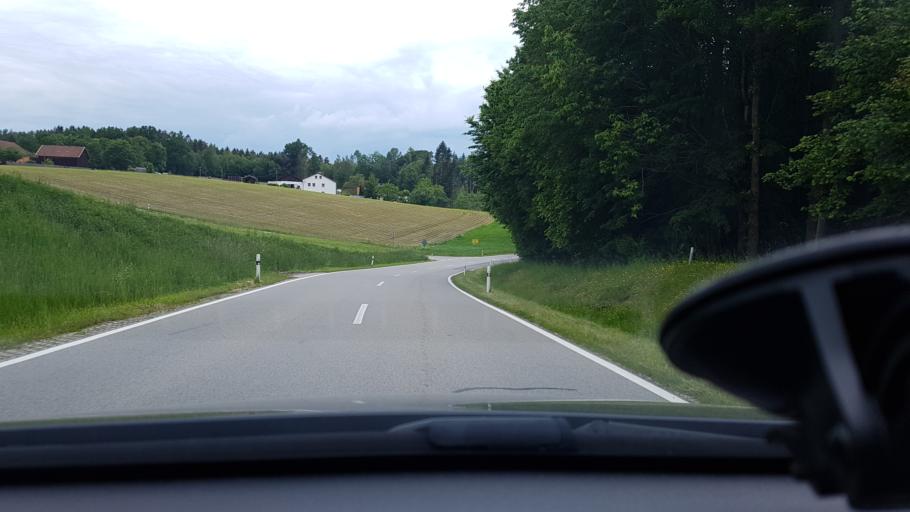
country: DE
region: Bavaria
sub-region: Lower Bavaria
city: Triftern
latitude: 48.3685
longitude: 13.0065
